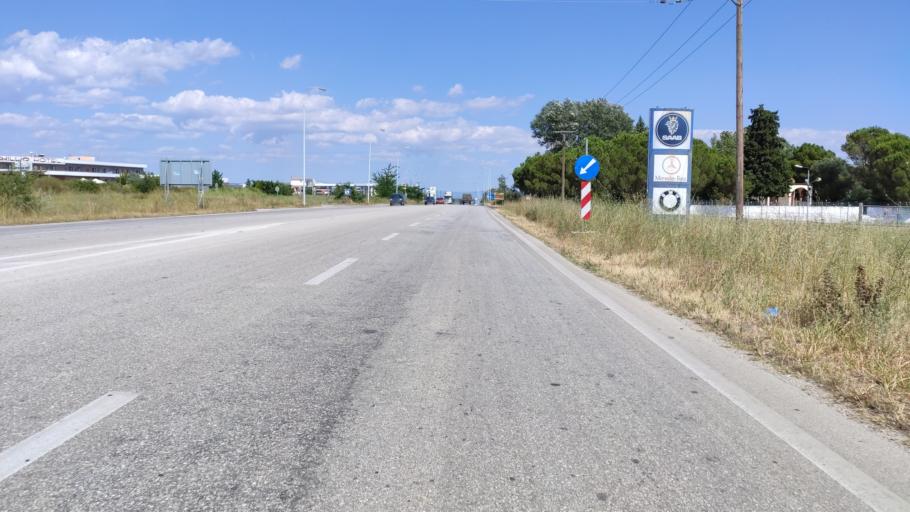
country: GR
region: East Macedonia and Thrace
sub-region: Nomos Rodopis
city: Komotini
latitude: 41.1084
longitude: 25.3508
